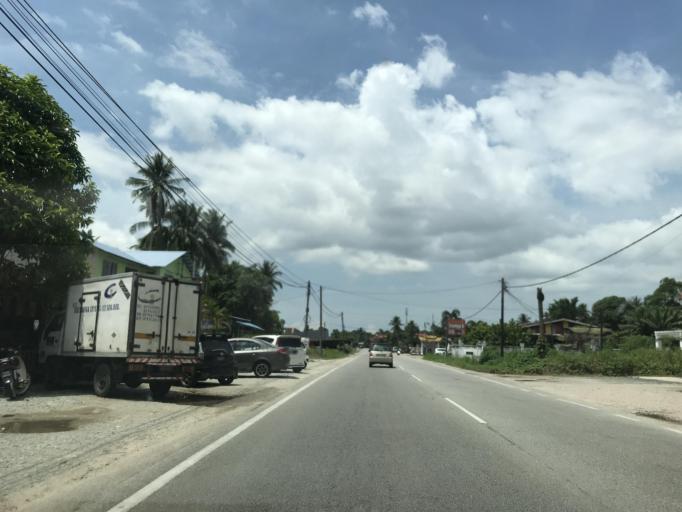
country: MY
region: Kelantan
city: Pasir Mas
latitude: 6.0588
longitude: 102.2006
